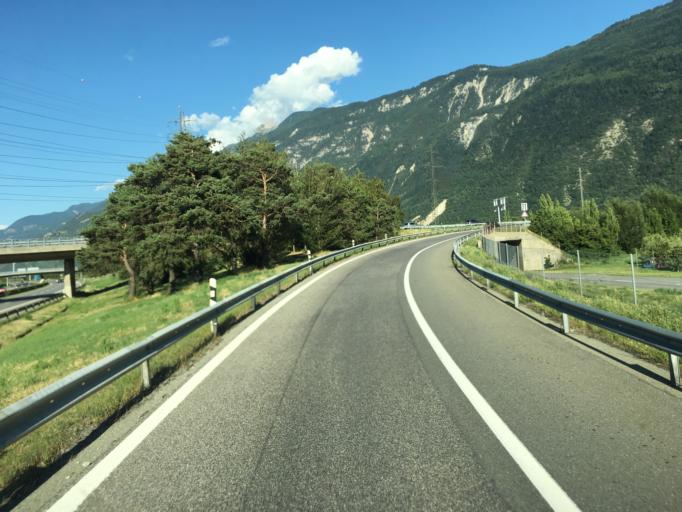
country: CH
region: Valais
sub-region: Martigny District
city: Martigny-Ville
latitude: 46.1140
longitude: 7.0945
